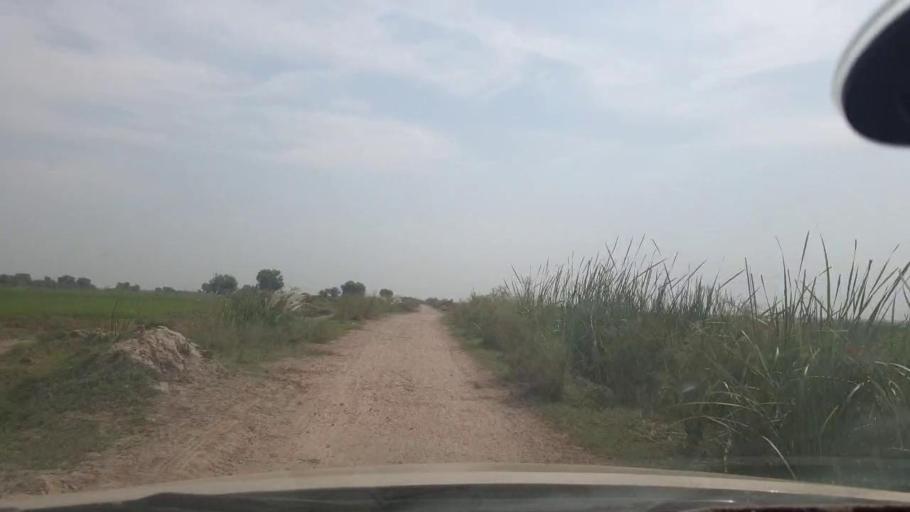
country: PK
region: Sindh
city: Jacobabad
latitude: 28.3176
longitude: 68.4874
